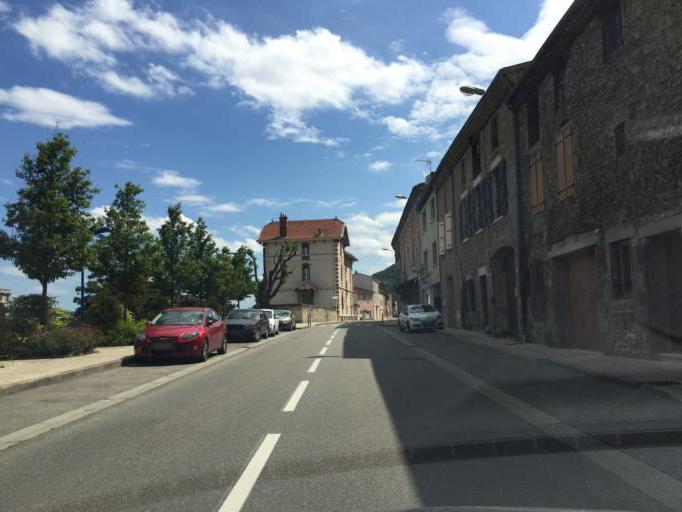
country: FR
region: Rhone-Alpes
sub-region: Departement de l'Ardeche
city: Andance
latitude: 45.2445
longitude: 4.8003
